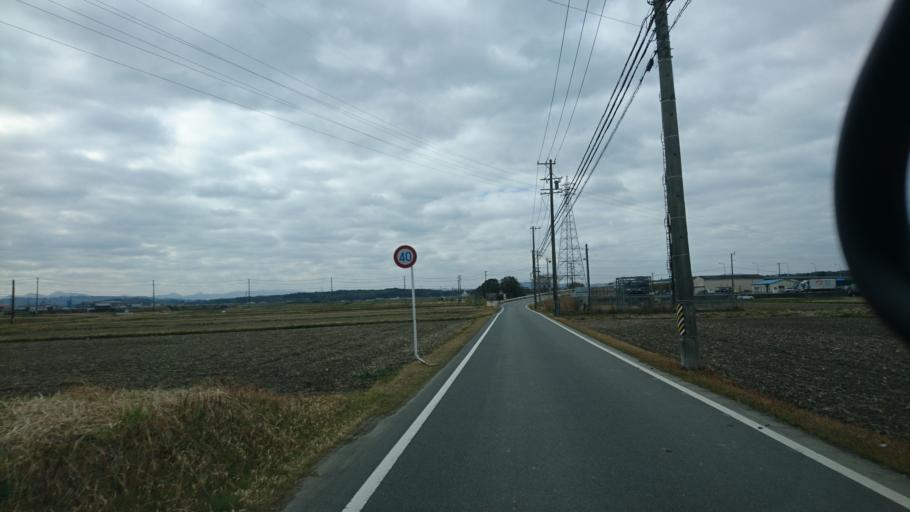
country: JP
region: Mie
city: Ueno-ebisumachi
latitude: 34.7532
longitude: 136.1200
